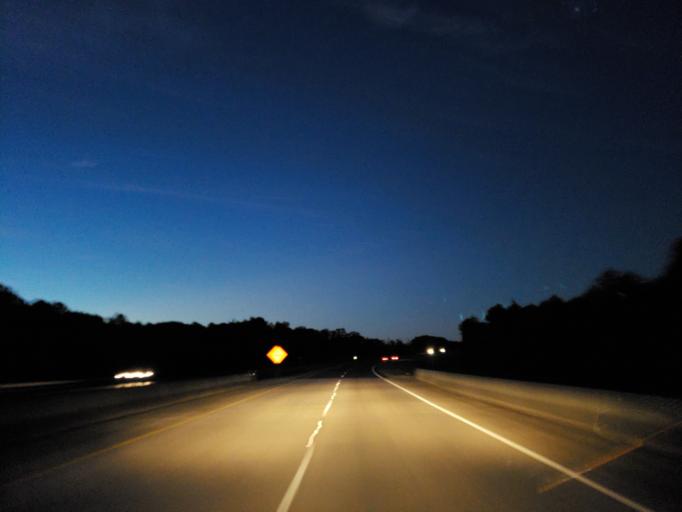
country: US
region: Mississippi
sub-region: Clarke County
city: Quitman
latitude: 32.1132
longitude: -88.7157
